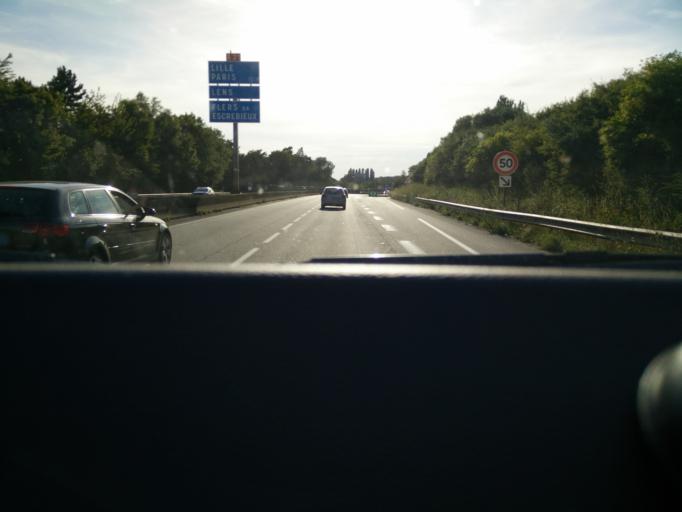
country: FR
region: Nord-Pas-de-Calais
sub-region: Departement du Nord
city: Roost-Warendin
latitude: 50.3988
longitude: 3.0942
